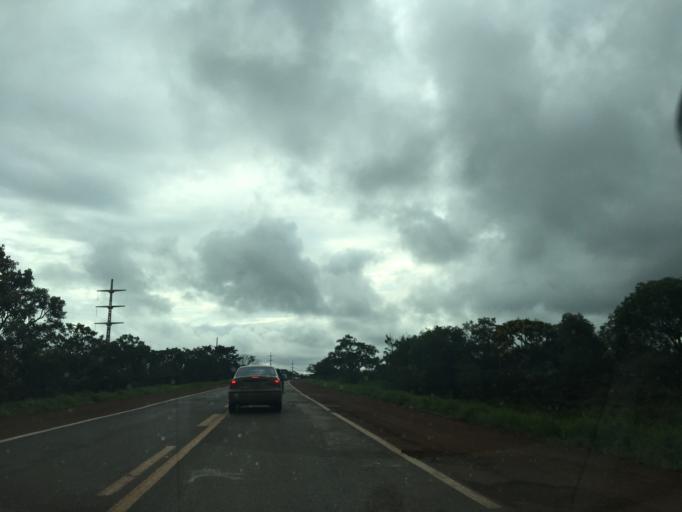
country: BR
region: Federal District
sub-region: Brasilia
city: Brasilia
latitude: -15.9823
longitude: -47.9280
